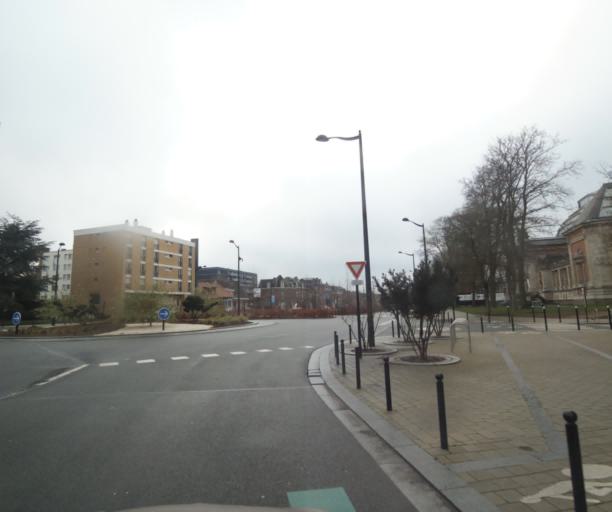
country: FR
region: Nord-Pas-de-Calais
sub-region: Departement du Nord
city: Valenciennes
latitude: 50.3584
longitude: 3.5319
